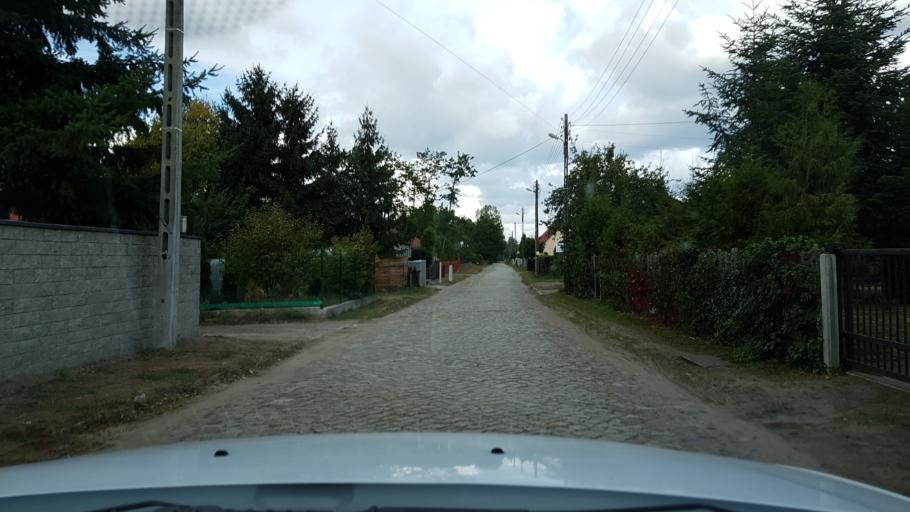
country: PL
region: West Pomeranian Voivodeship
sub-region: Powiat gryfinski
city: Gryfino
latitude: 53.2921
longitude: 14.5005
